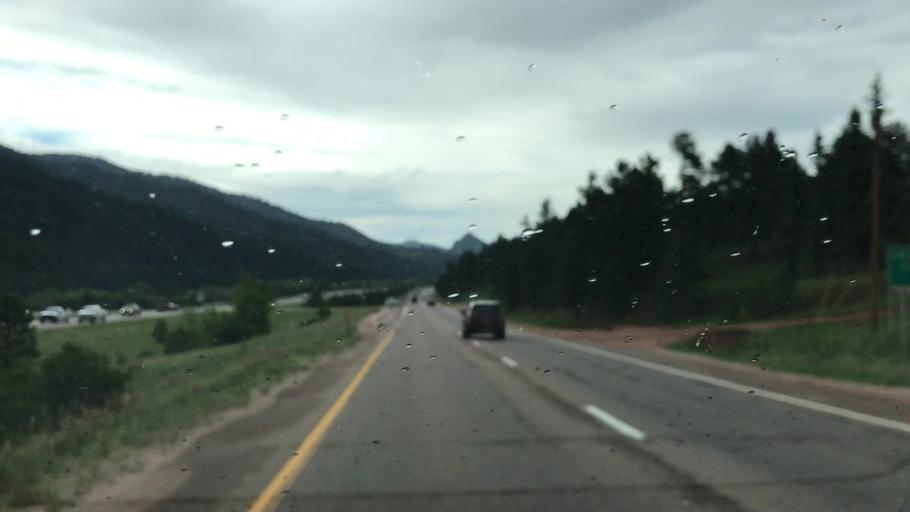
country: US
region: Colorado
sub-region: El Paso County
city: Cascade-Chipita Park
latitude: 38.9411
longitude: -105.0149
